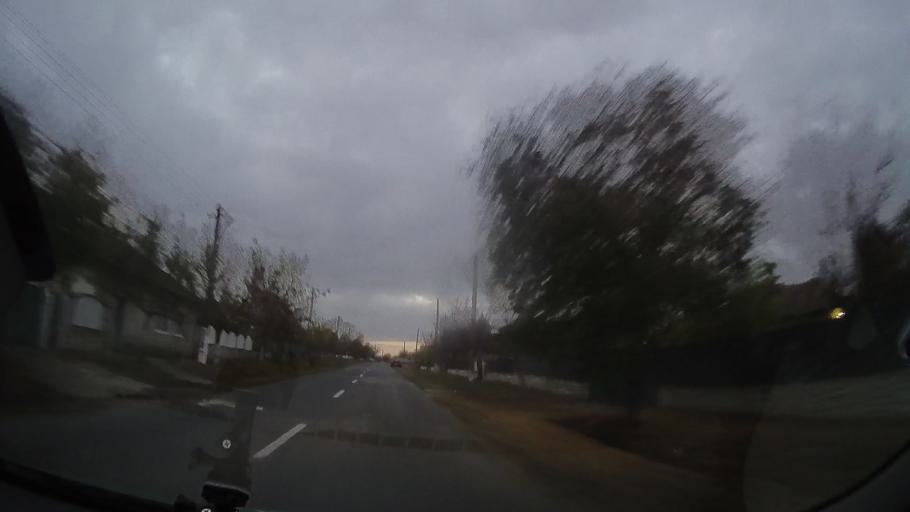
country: RO
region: Tulcea
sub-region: Comuna Mihai Bravu
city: Turda
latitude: 44.9748
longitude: 28.6230
